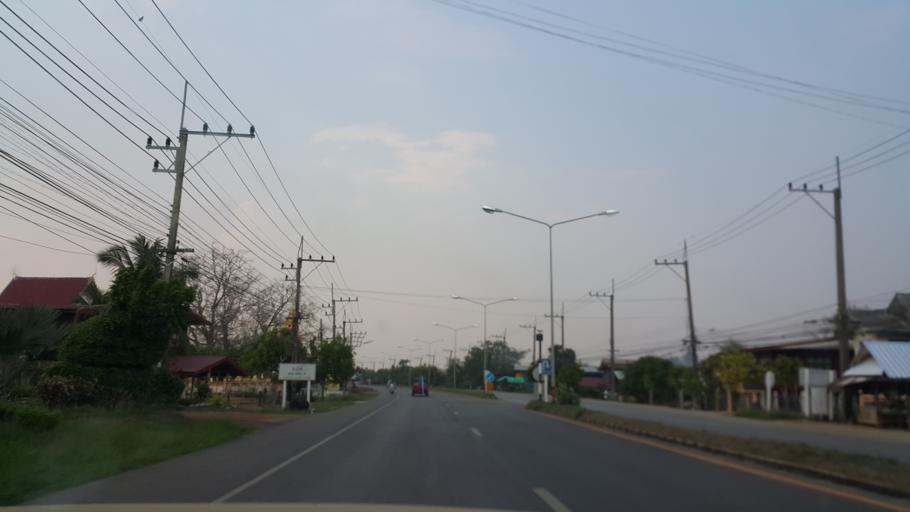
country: TH
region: Nakhon Phanom
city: That Phanom
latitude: 16.9872
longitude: 104.7267
